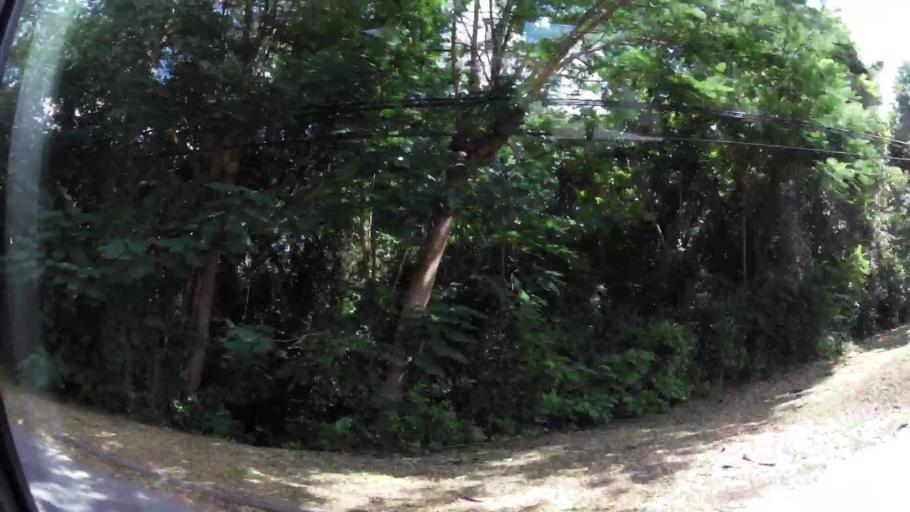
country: BB
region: Saint James
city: Holetown
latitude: 13.2160
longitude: -59.6161
